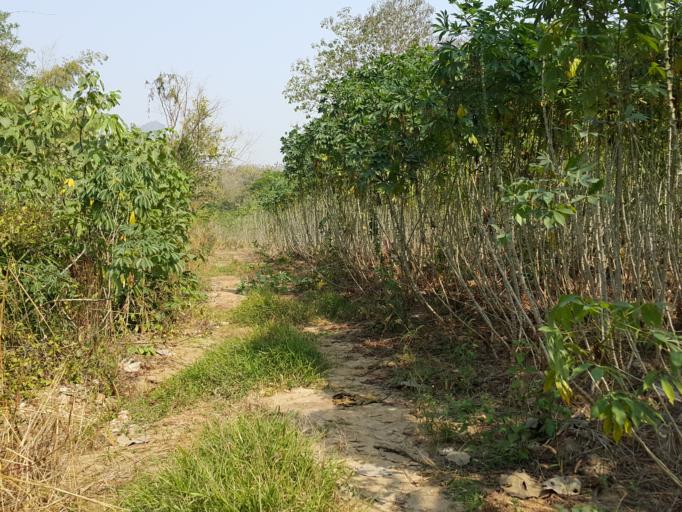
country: TH
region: Sukhothai
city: Thung Saliam
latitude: 17.3279
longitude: 99.4890
